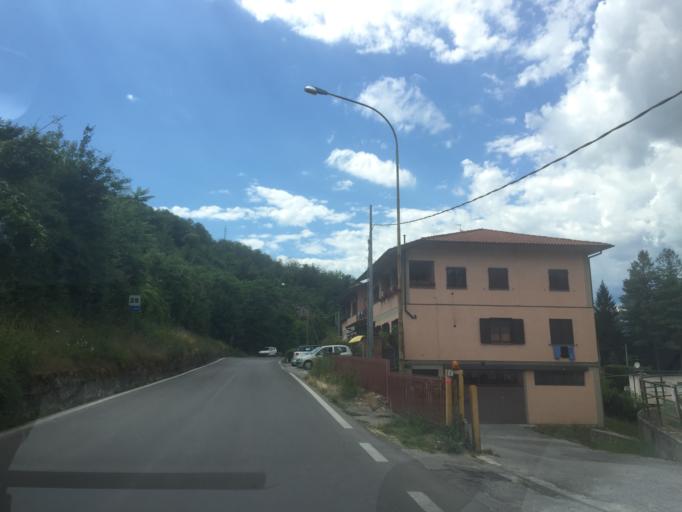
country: IT
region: Tuscany
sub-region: Provincia di Lucca
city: Castelnuovo di Garfagnana
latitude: 44.1134
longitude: 10.4006
